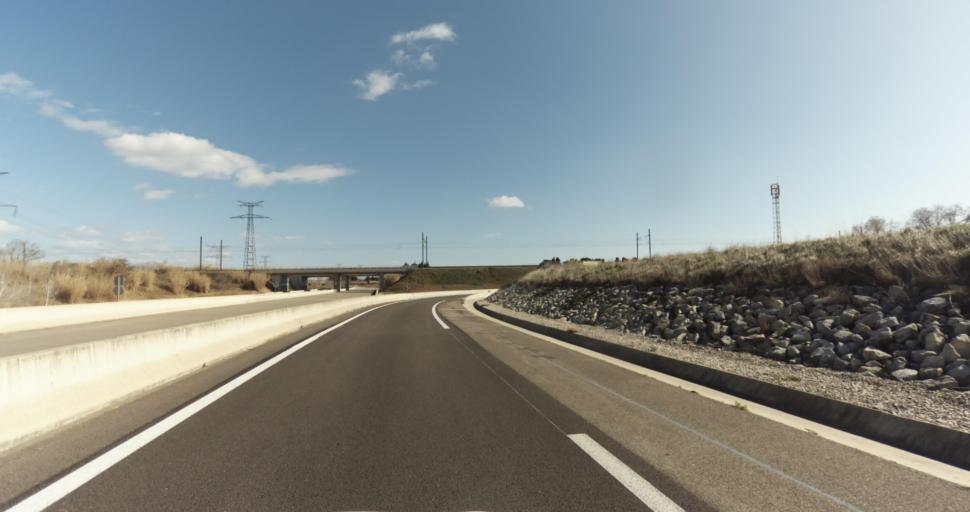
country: FR
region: Provence-Alpes-Cote d'Azur
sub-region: Departement des Bouches-du-Rhone
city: Rognonas
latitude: 43.9137
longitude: 4.7909
